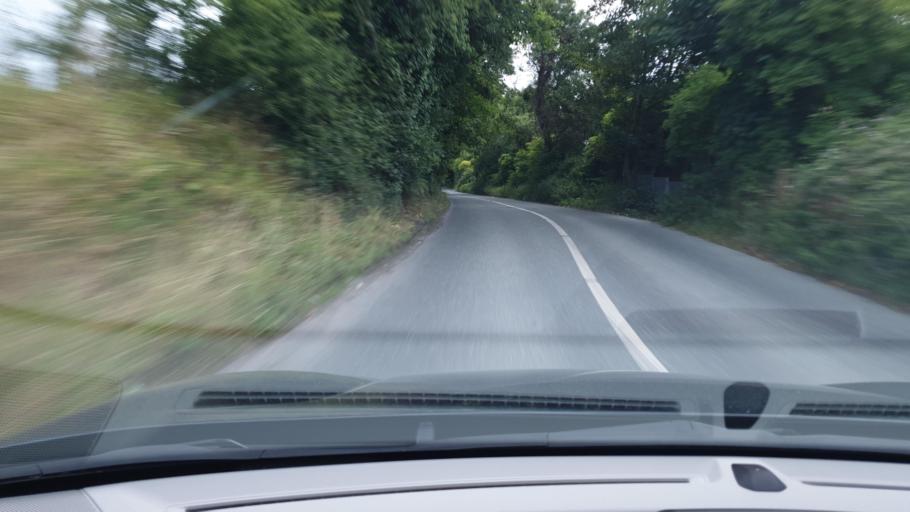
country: IE
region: Leinster
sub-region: South Dublin
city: Saggart
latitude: 53.2751
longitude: -6.4274
